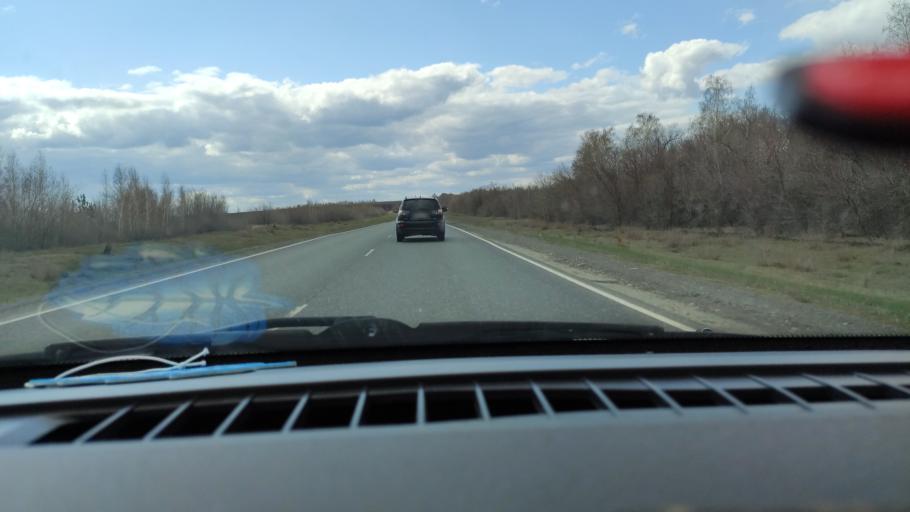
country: RU
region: Saratov
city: Balakovo
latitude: 52.1367
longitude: 47.7965
